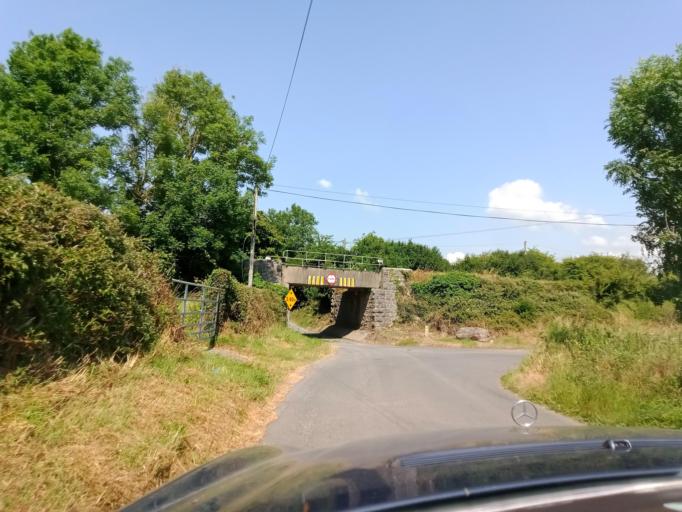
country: IE
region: Leinster
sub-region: Kilkenny
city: Mooncoin
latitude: 52.3109
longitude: -7.2712
